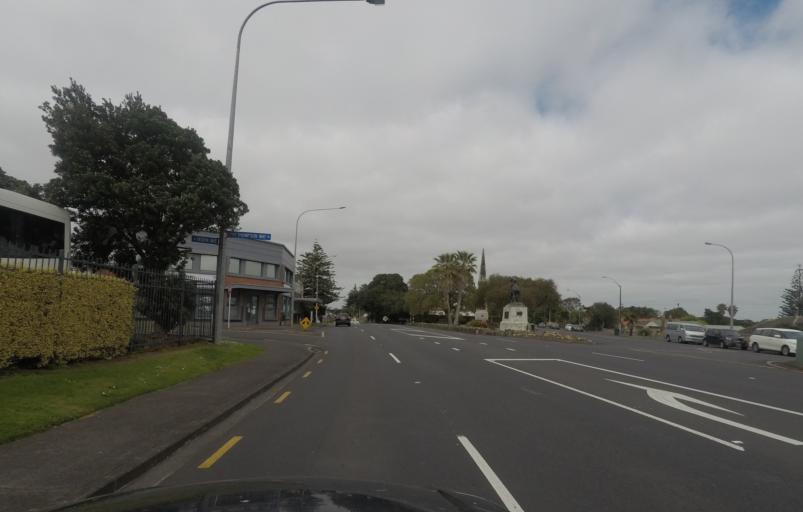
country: NZ
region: Auckland
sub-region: Auckland
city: Mangere
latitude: -36.9495
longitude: 174.8453
